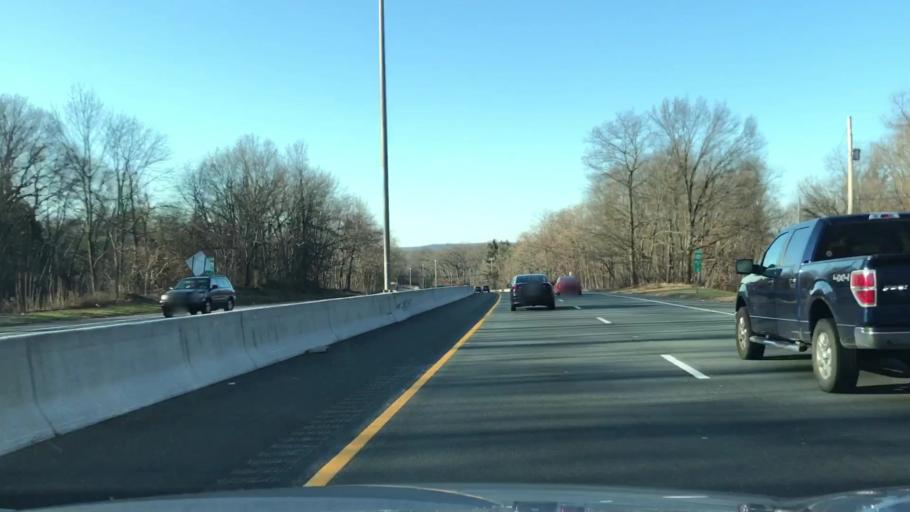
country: US
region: New Jersey
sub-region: Bergen County
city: Wyckoff
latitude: 41.0057
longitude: -74.1903
